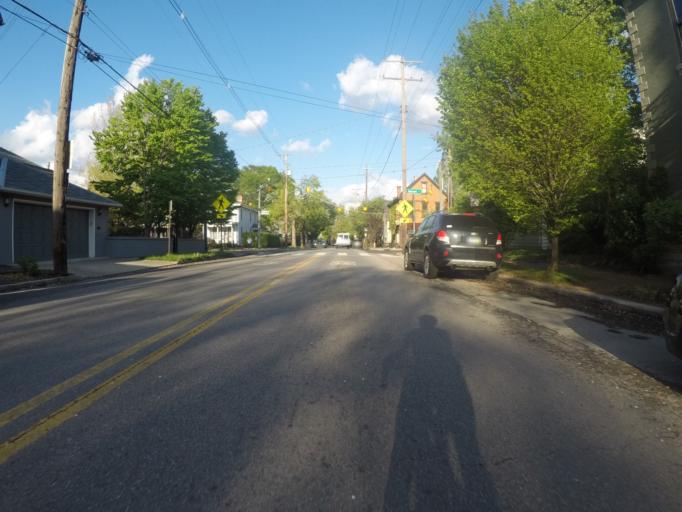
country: US
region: Ohio
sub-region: Franklin County
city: Columbus
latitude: 39.9443
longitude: -82.9932
